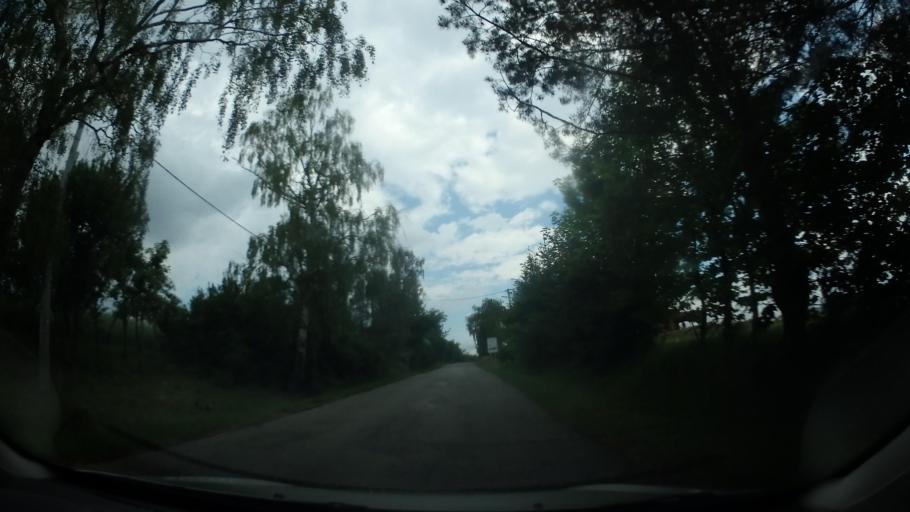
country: CZ
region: South Moravian
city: Boritov
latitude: 49.4513
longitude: 16.5990
